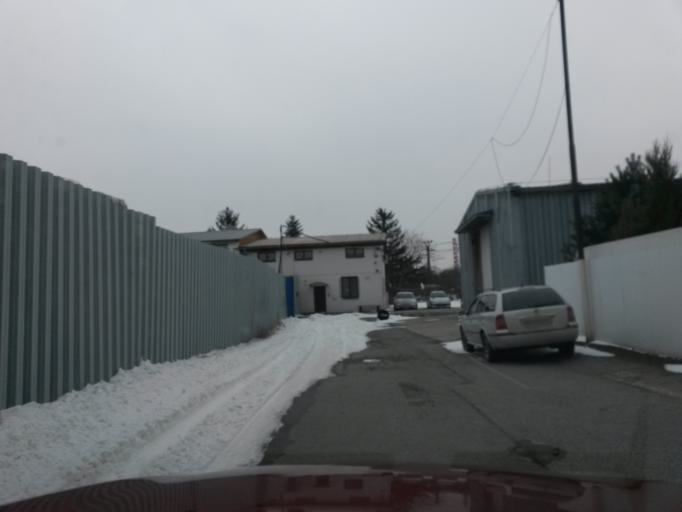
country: SK
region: Kosicky
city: Kosice
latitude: 48.7077
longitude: 21.2693
